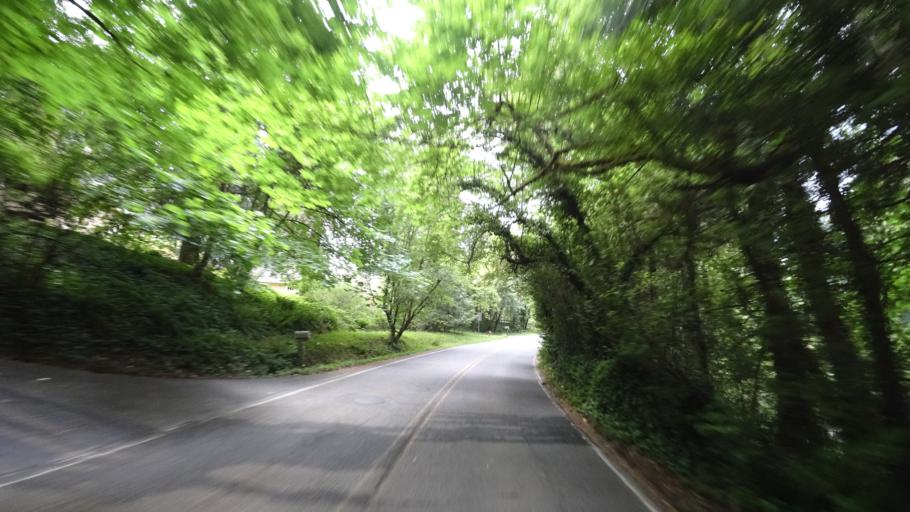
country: US
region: Oregon
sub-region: Clackamas County
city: Lake Oswego
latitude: 45.4572
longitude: -122.7015
